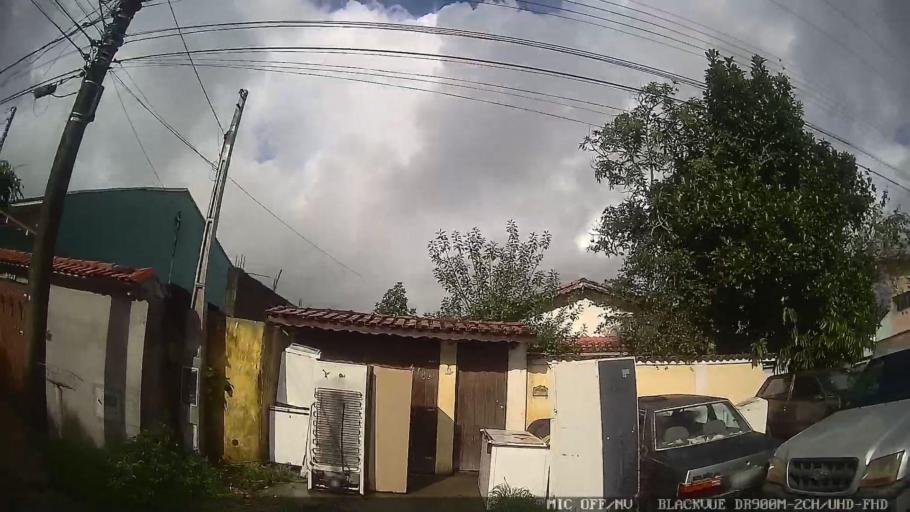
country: BR
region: Sao Paulo
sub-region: Itanhaem
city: Itanhaem
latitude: -24.2213
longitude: -46.8872
